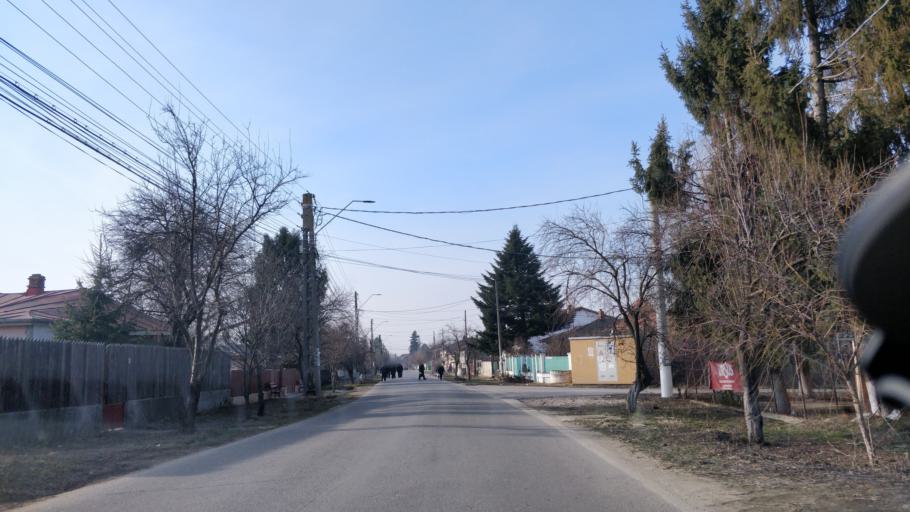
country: RO
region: Giurgiu
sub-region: Comuna Ulmi
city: Trestieni
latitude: 44.5011
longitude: 25.7629
